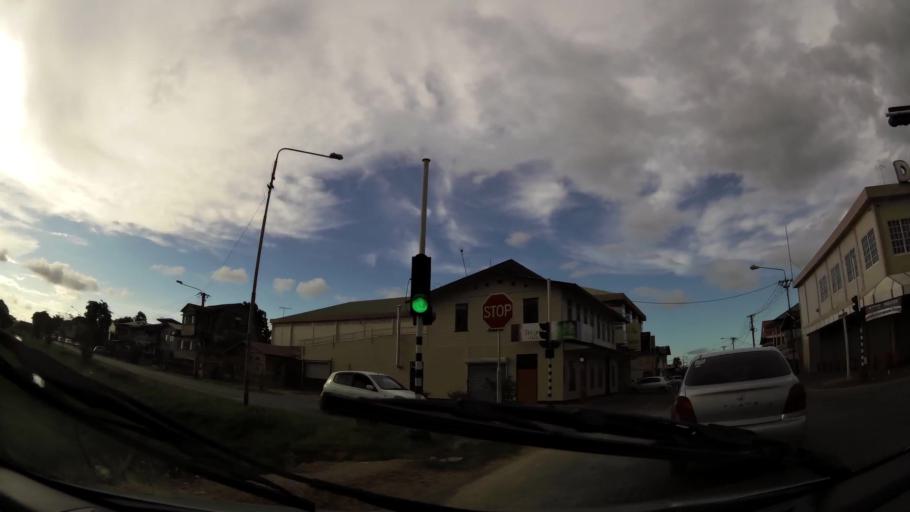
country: SR
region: Paramaribo
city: Paramaribo
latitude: 5.8313
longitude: -55.1737
